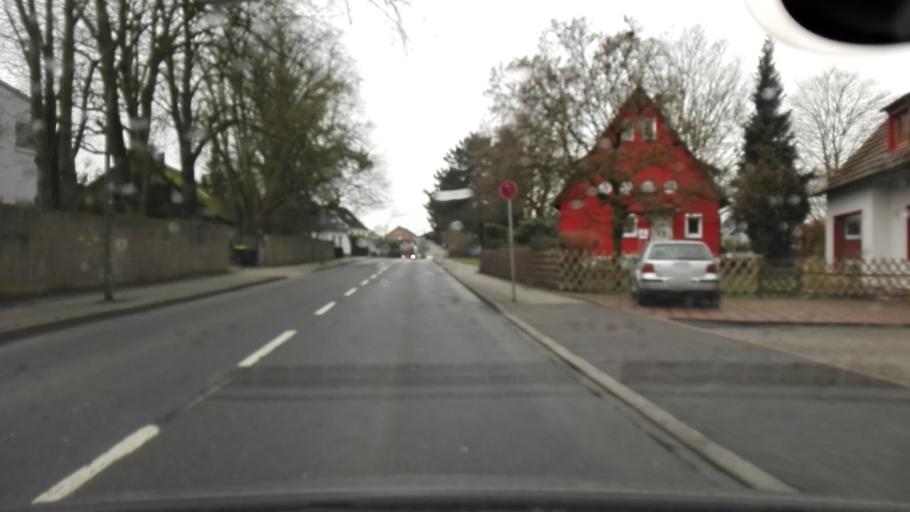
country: DE
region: North Rhine-Westphalia
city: Kamen
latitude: 51.5842
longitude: 7.6561
